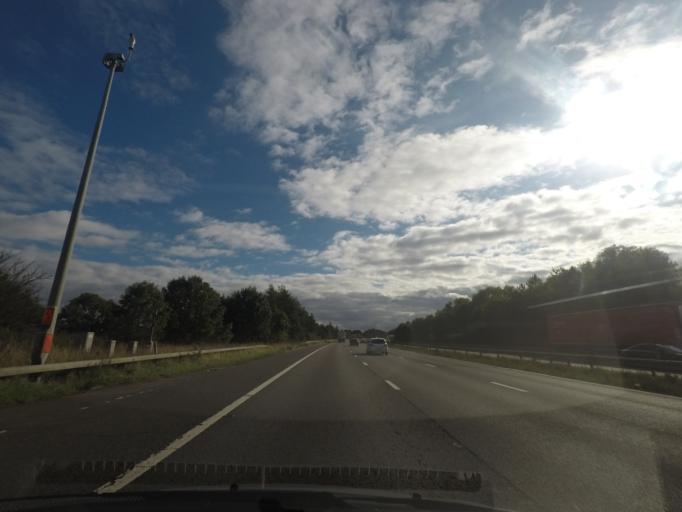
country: GB
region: England
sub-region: Leicestershire
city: Markfield
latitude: 52.7229
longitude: -1.2829
